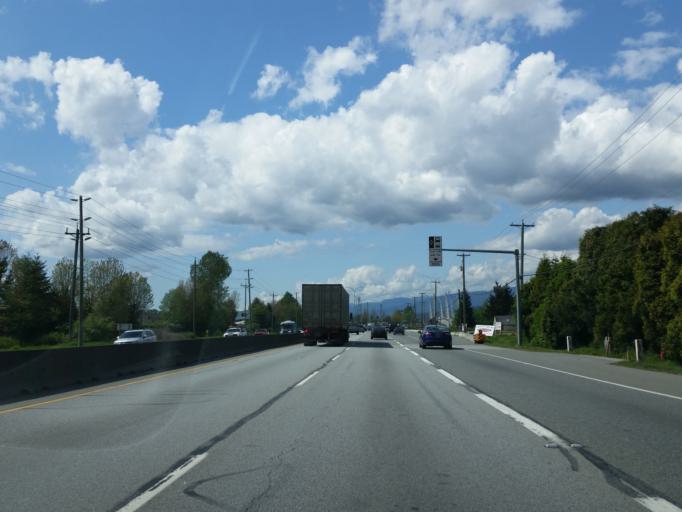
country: CA
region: British Columbia
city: Pitt Meadows
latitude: 49.2408
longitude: -122.7142
